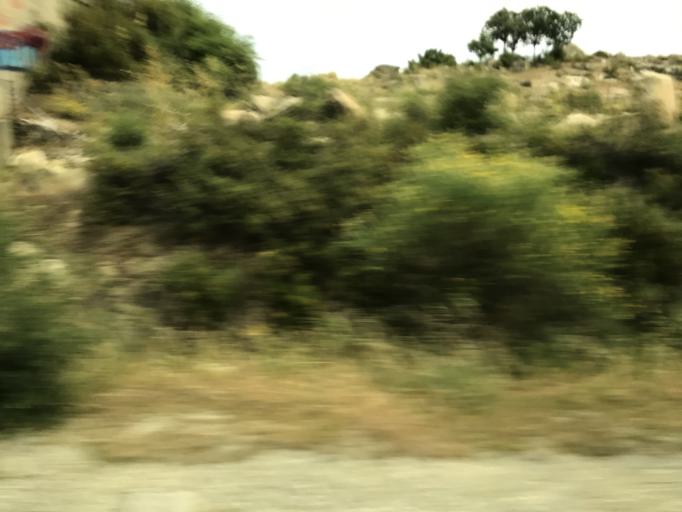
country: ES
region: Madrid
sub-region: Provincia de Madrid
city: La Cabrera
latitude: 40.8907
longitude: -3.6012
